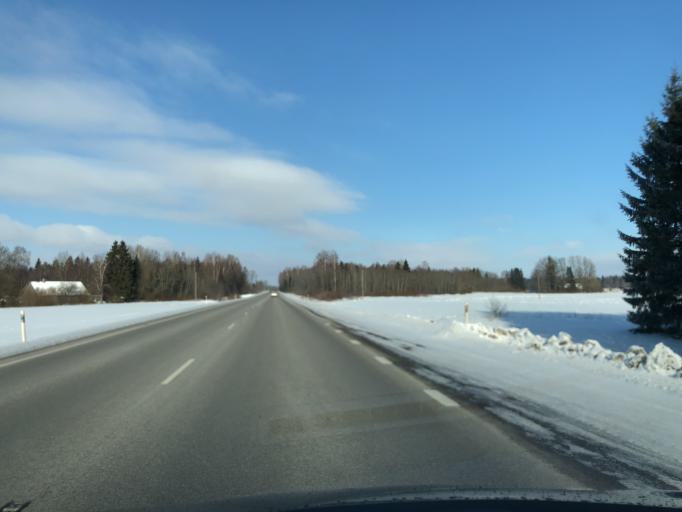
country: EE
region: Jaervamaa
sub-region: Paide linn
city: Paide
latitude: 58.8064
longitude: 25.7578
